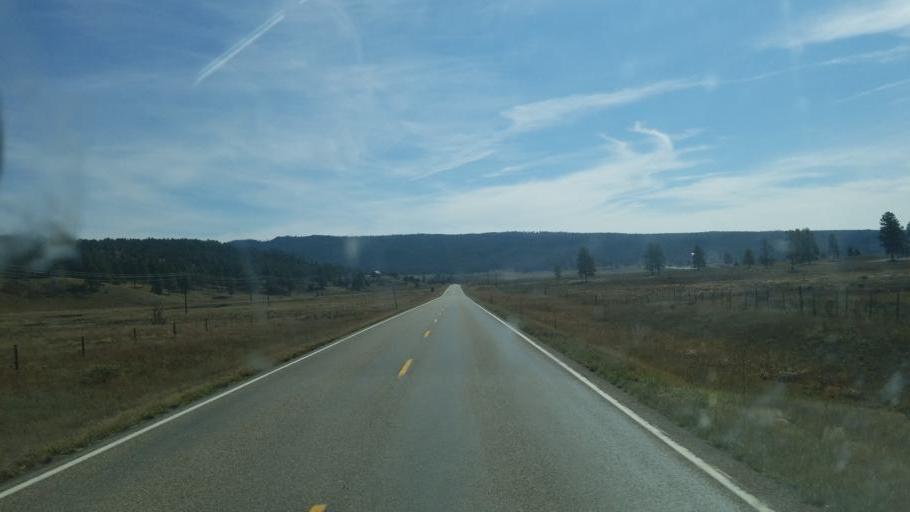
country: US
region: New Mexico
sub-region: Rio Arriba County
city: Dulce
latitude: 37.0925
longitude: -106.9082
